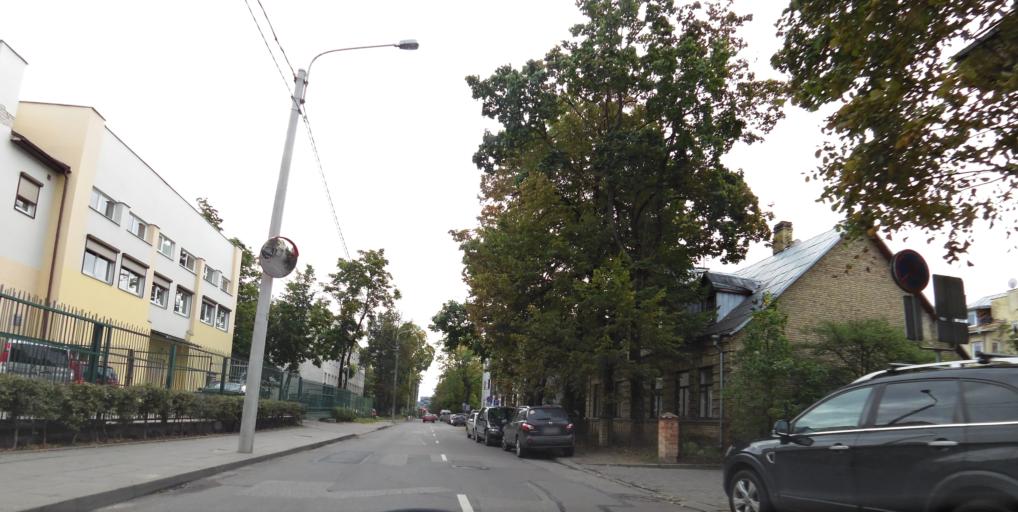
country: LT
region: Vilnius County
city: Seskine
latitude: 54.6971
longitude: 25.2538
